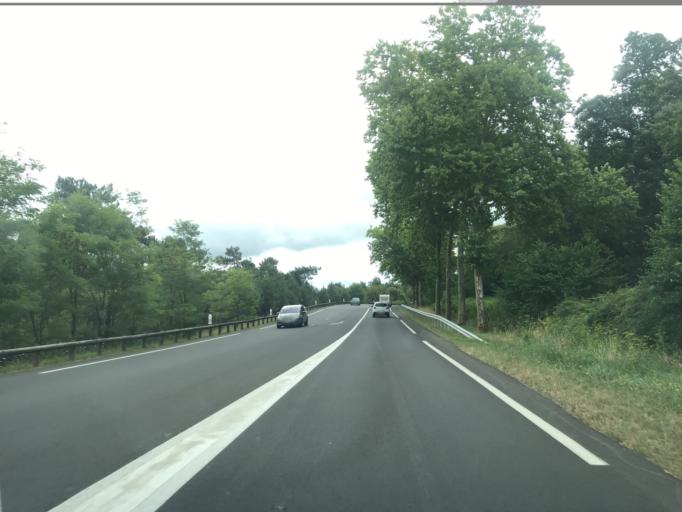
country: FR
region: Poitou-Charentes
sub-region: Departement de la Charente
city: Dignac
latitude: 45.5276
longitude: 0.2927
